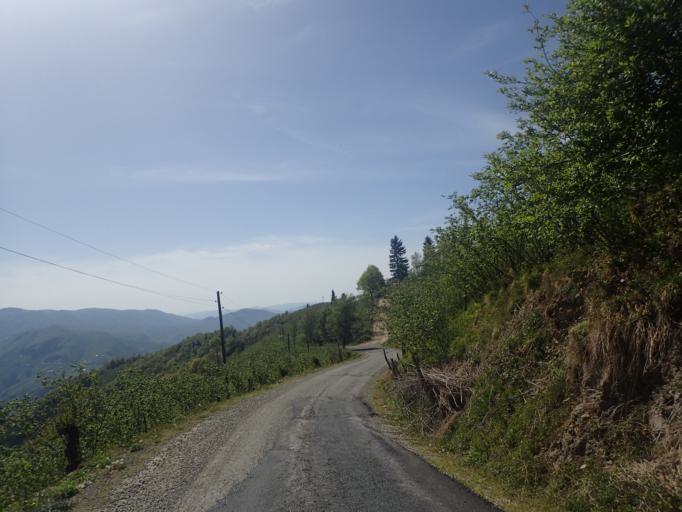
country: TR
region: Ordu
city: Kabaduz
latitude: 40.8037
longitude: 37.9013
